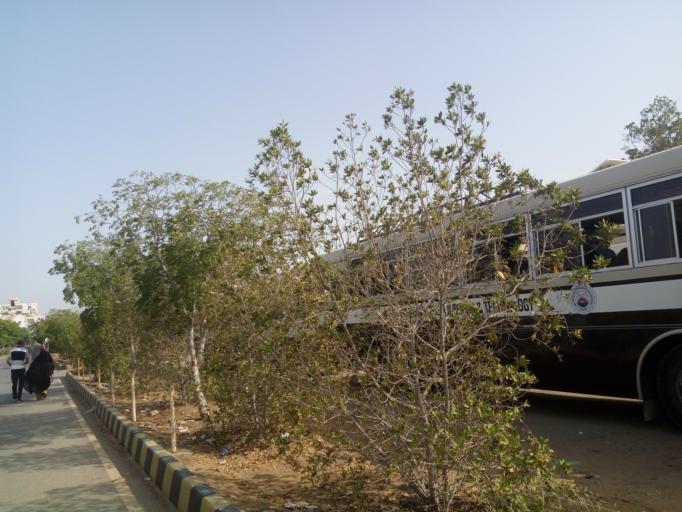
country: PK
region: Sindh
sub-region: Karachi District
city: Karachi
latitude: 24.9320
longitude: 67.1142
